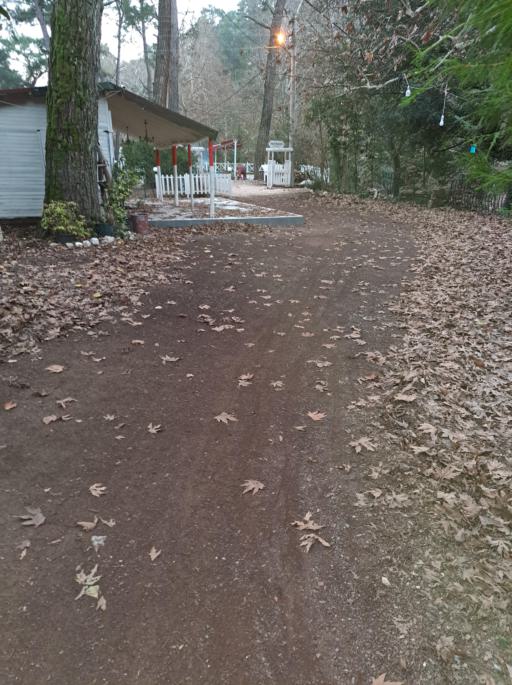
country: TR
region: Antalya
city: Tekirova
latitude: 36.4232
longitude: 30.4532
